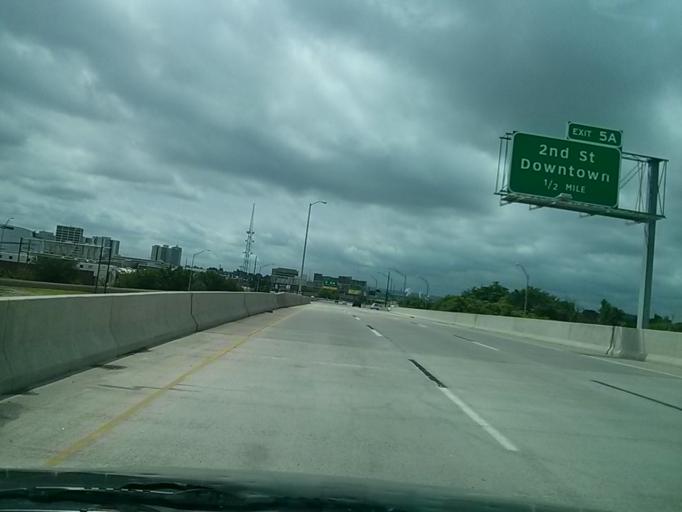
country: US
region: Oklahoma
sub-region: Tulsa County
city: Tulsa
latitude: 36.1583
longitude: -96.0020
